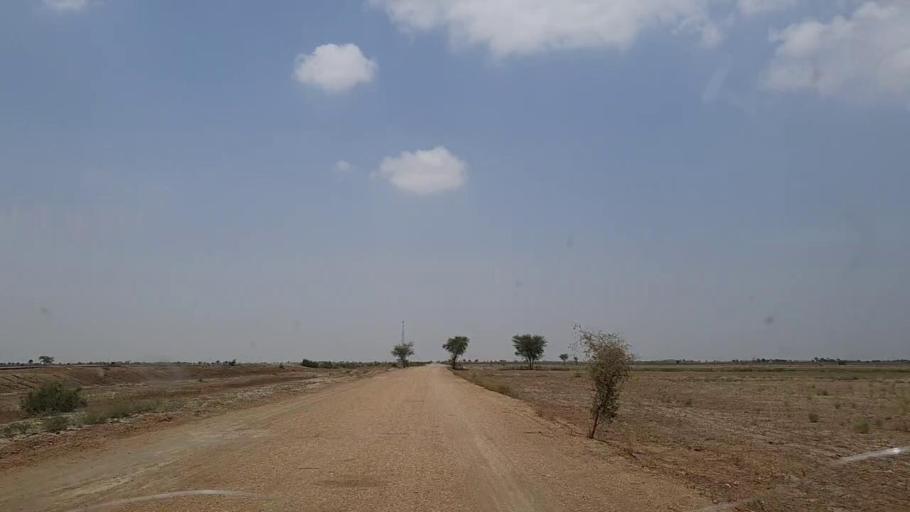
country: PK
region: Sindh
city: Johi
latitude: 26.7784
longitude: 67.6517
